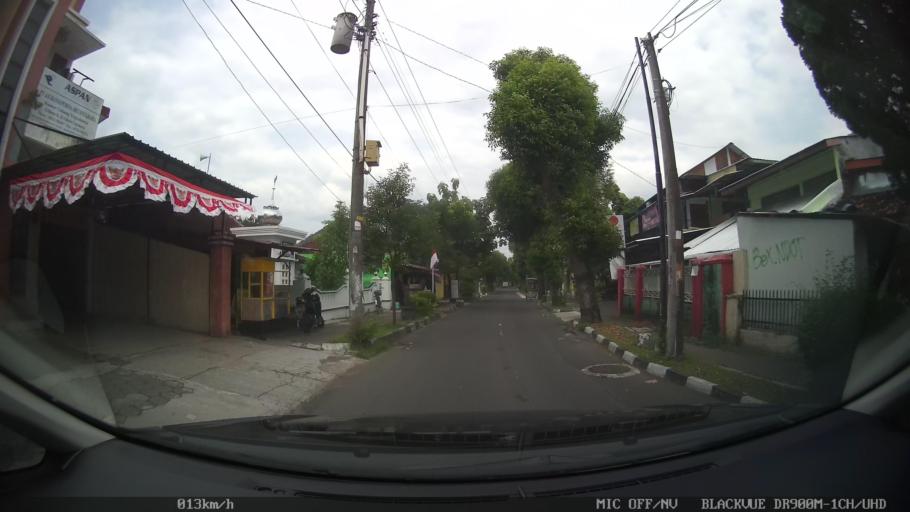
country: ID
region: Daerah Istimewa Yogyakarta
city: Yogyakarta
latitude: -7.7914
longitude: 110.3845
